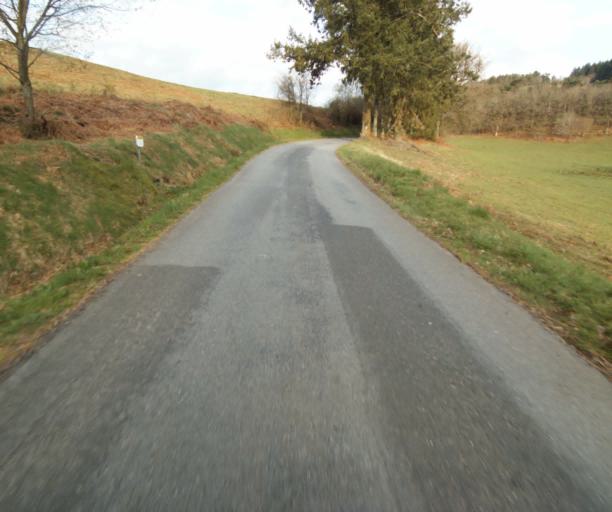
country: FR
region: Limousin
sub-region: Departement de la Correze
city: Correze
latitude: 45.4140
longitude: 1.9103
